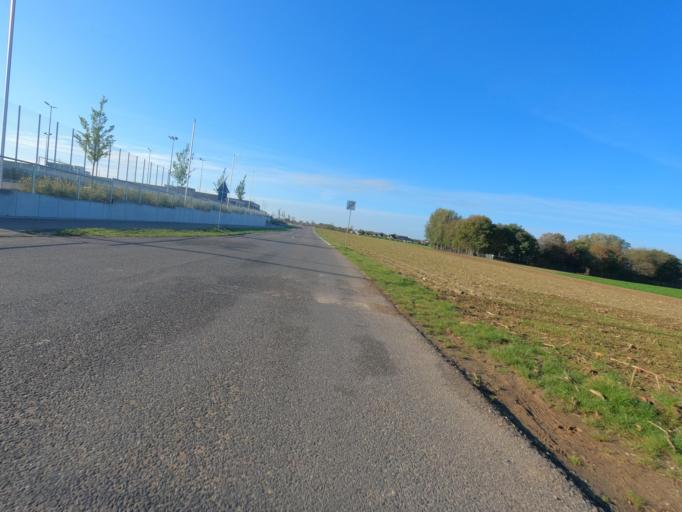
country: DE
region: North Rhine-Westphalia
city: Erkelenz
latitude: 51.0946
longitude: 6.3380
